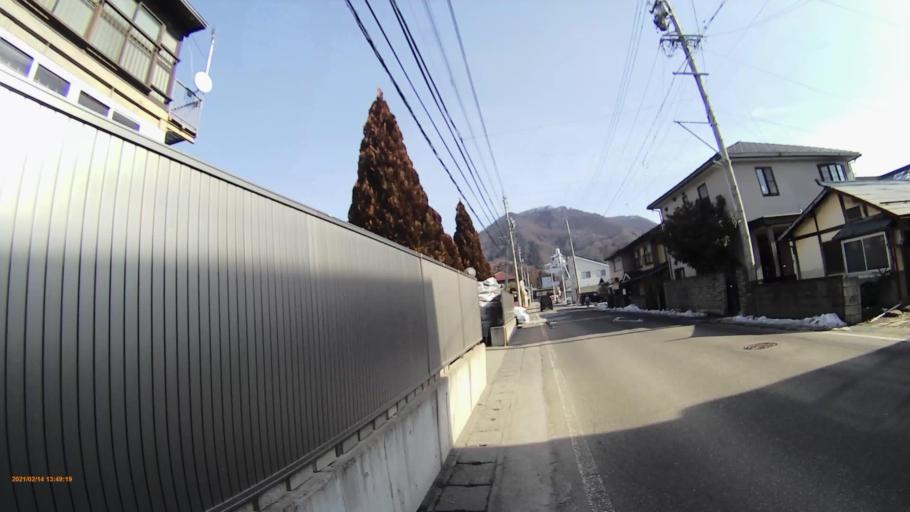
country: JP
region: Nagano
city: Nakano
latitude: 36.7495
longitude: 138.3762
